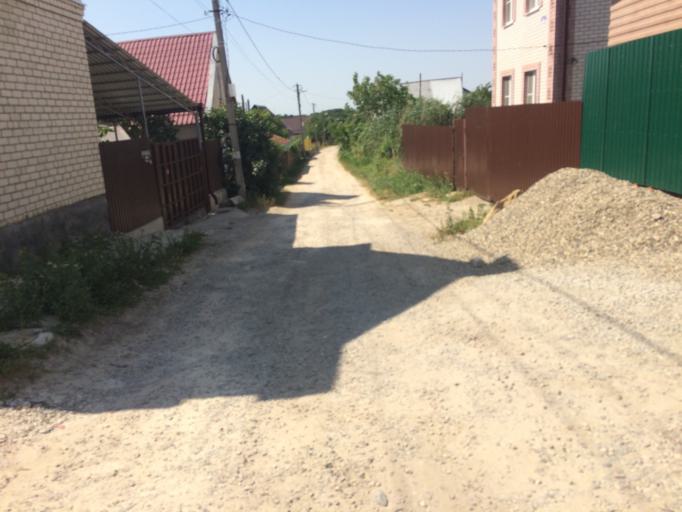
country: RU
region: Stavropol'skiy
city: Tatarka
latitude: 44.9829
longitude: 41.9413
